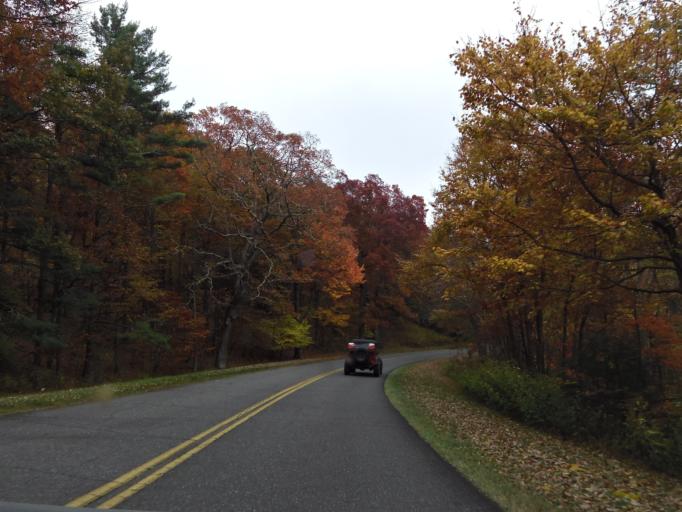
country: US
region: North Carolina
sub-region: Ashe County
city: West Jefferson
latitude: 36.2418
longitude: -81.4824
